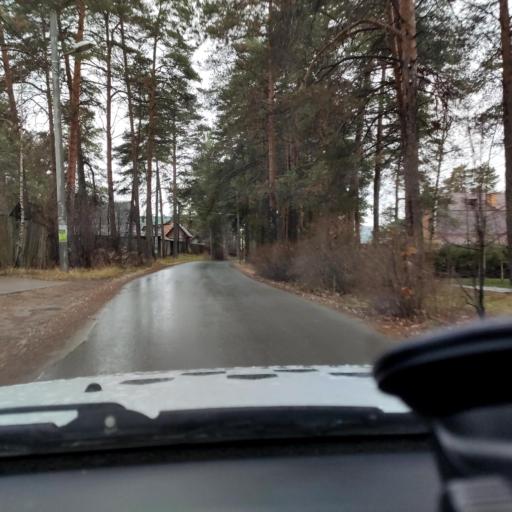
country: RU
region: Perm
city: Perm
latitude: 58.0564
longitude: 56.3003
